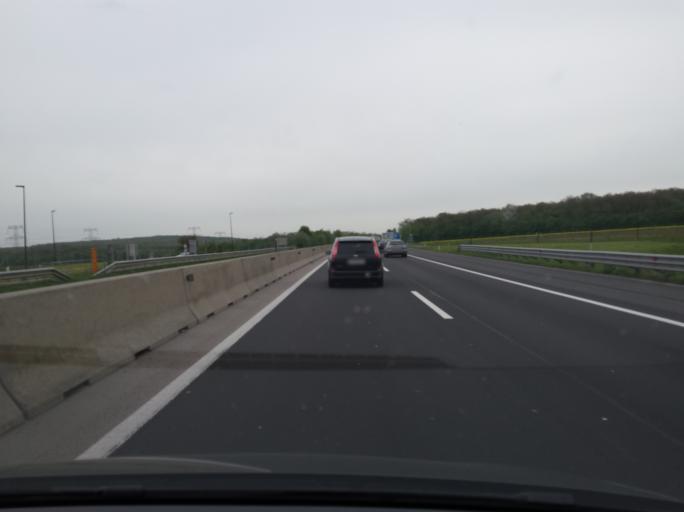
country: AT
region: Lower Austria
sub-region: Politischer Bezirk Wien-Umgebung
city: Fischamend Dorf
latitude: 48.0942
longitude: 16.6613
